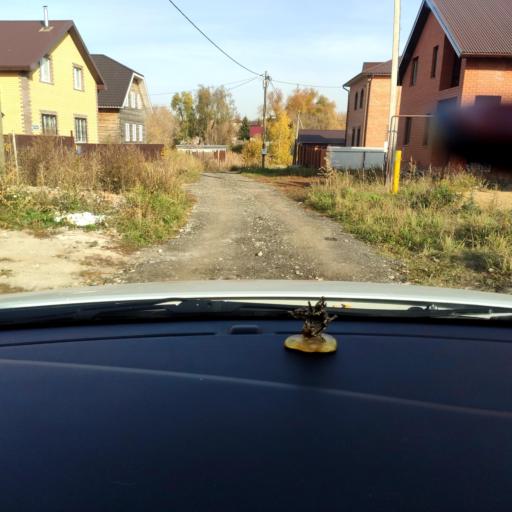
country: RU
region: Tatarstan
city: Vysokaya Gora
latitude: 55.7957
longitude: 49.2714
